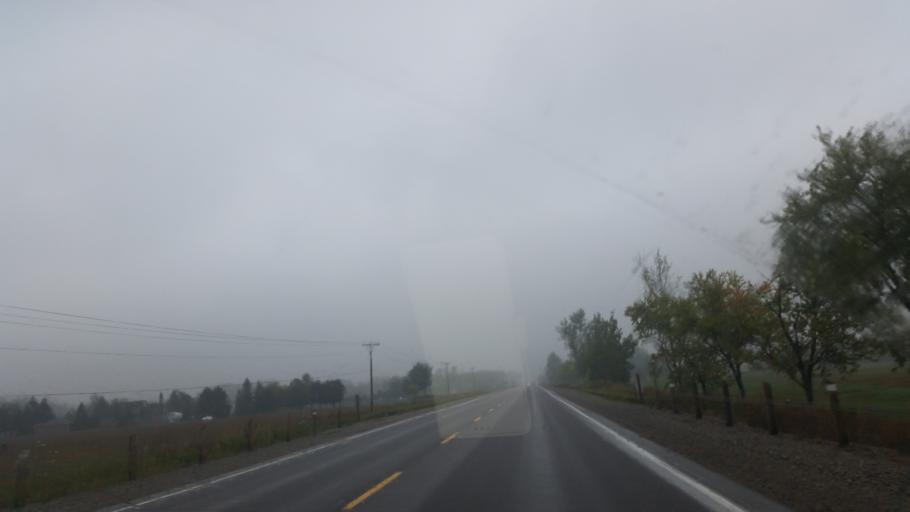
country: CA
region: Ontario
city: Stratford
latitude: 43.2913
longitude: -81.0500
